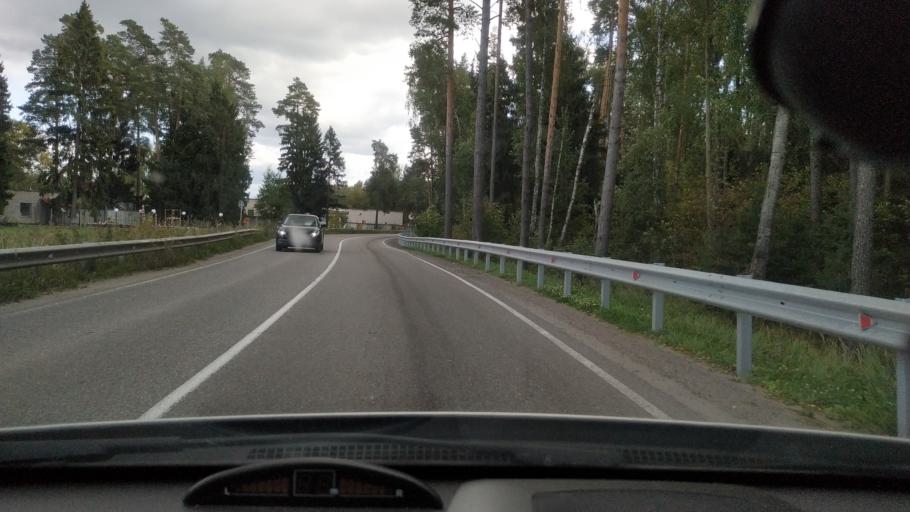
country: RU
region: Moskovskaya
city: Zheleznodorozhnyy
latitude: 55.7923
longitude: 38.0348
